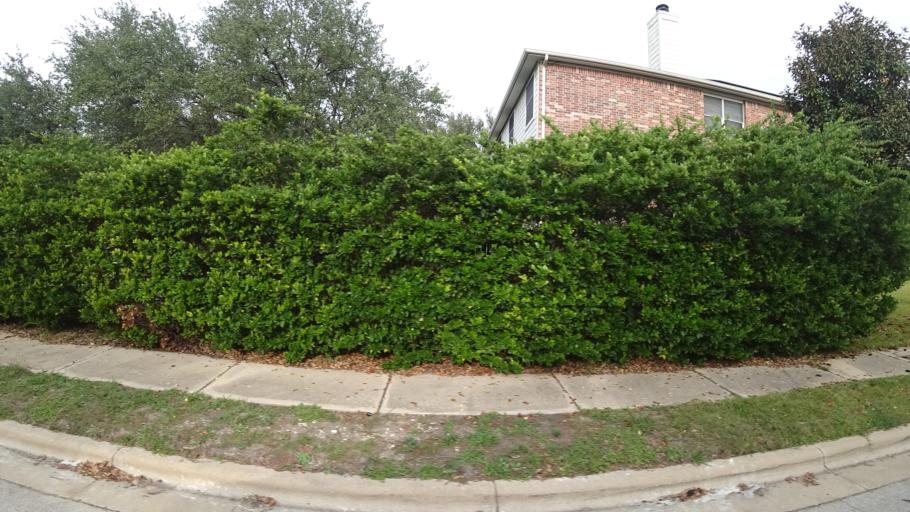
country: US
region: Texas
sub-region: Travis County
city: Hudson Bend
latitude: 30.3799
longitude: -97.8865
